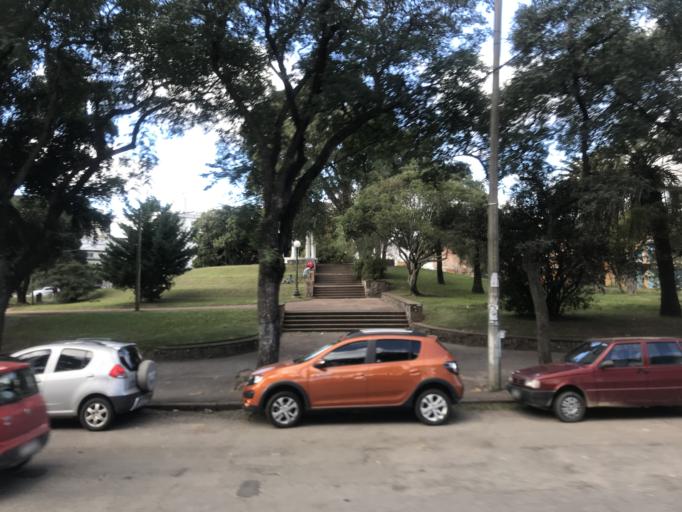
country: UY
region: Montevideo
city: Montevideo
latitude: -34.9120
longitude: -56.1660
